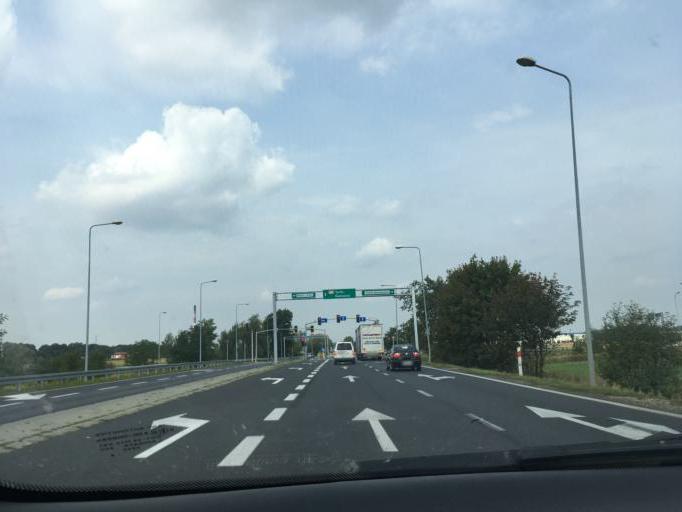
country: PL
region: Silesian Voivodeship
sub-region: Powiat bierunsko-ledzinski
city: Bierun
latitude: 50.0917
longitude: 19.1050
